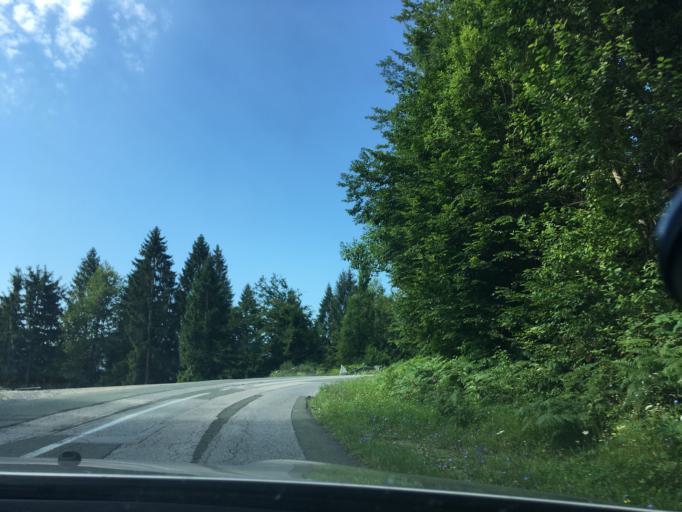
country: HR
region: Primorsko-Goranska
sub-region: Grad Delnice
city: Delnice
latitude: 45.4316
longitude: 14.8460
